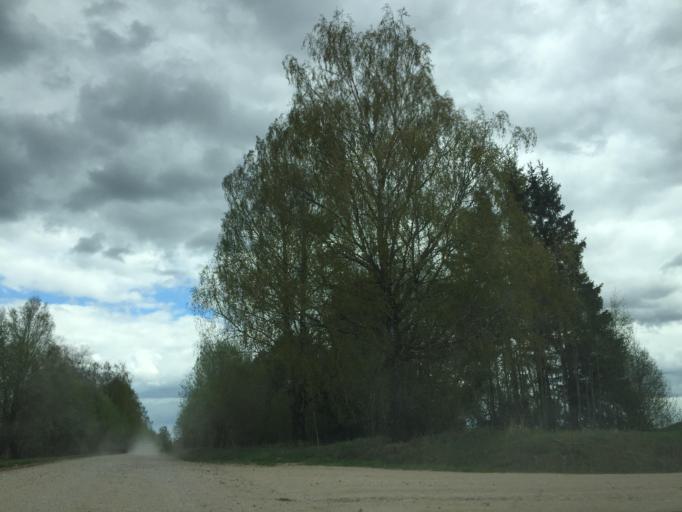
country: LV
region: Madonas Rajons
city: Madona
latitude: 56.9243
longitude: 26.0397
